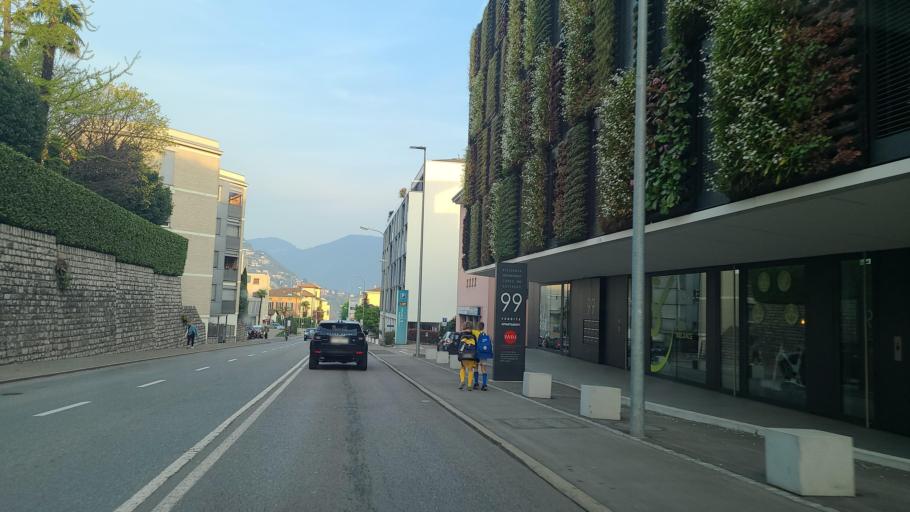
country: CH
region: Ticino
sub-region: Lugano District
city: Massagno
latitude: 46.0138
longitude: 8.9426
